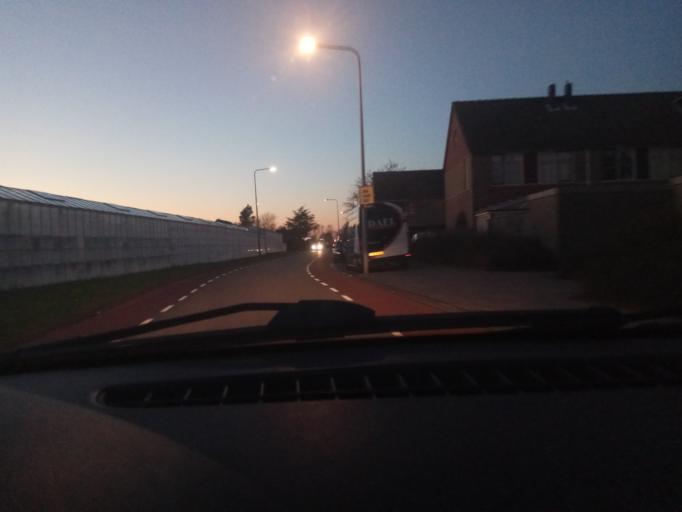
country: NL
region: South Holland
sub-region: Gemeente Westland
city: Maasdijk
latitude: 51.9554
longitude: 4.2131
